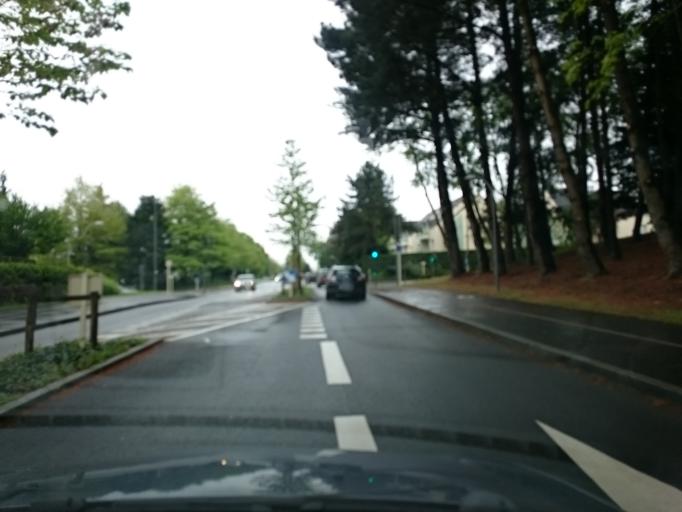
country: FR
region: Brittany
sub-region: Departement d'Ille-et-Vilaine
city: Saint-Gregoire
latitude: 48.1463
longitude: -1.6863
